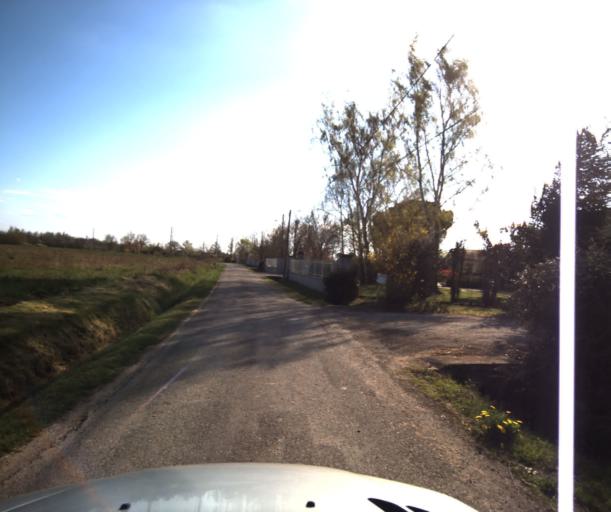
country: FR
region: Midi-Pyrenees
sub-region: Departement du Tarn-et-Garonne
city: Bressols
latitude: 43.9470
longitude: 1.3114
